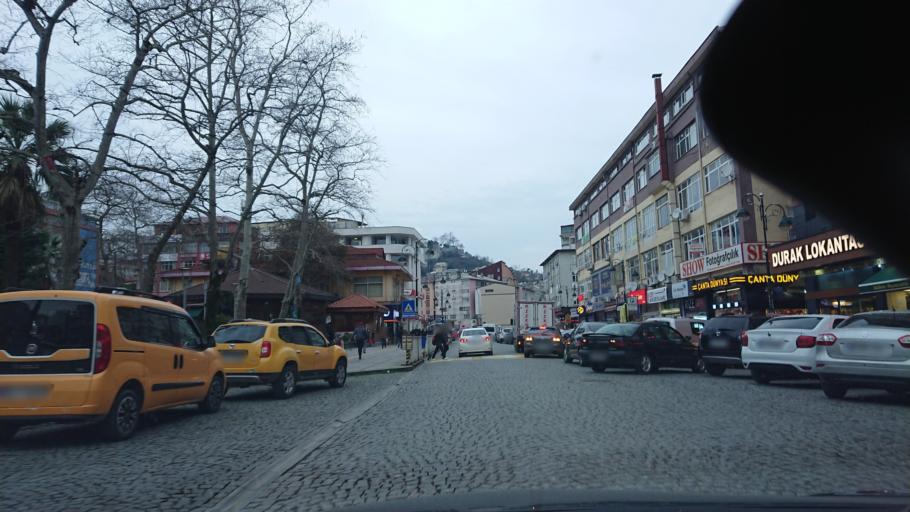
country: TR
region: Rize
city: Rize
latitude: 41.0252
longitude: 40.5187
